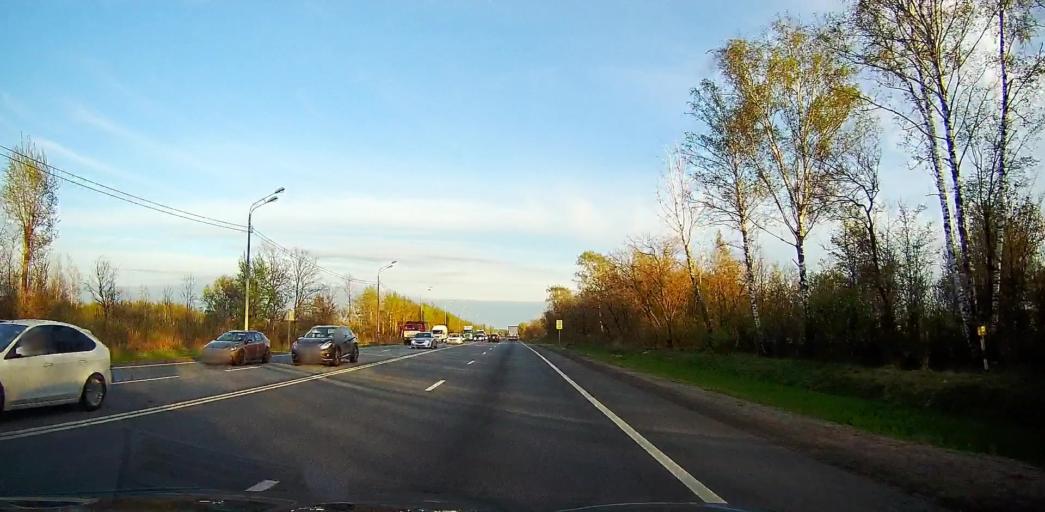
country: RU
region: Moskovskaya
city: Troitskoye
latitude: 55.2692
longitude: 38.5007
